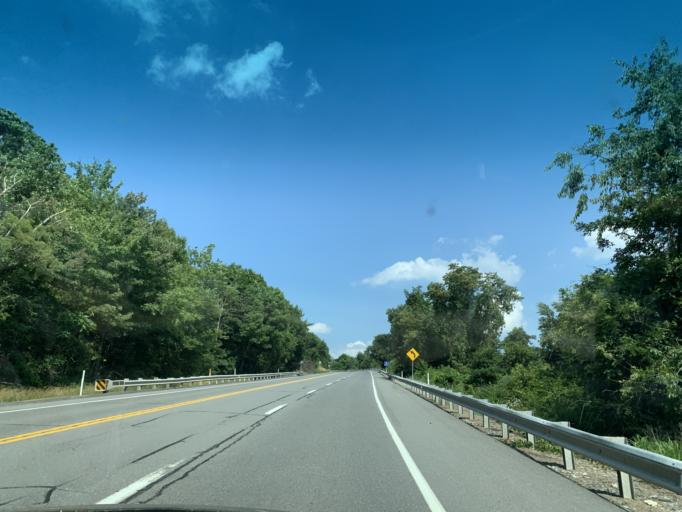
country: US
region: Pennsylvania
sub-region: Schuylkill County
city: Ashland
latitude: 40.8088
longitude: -76.3392
